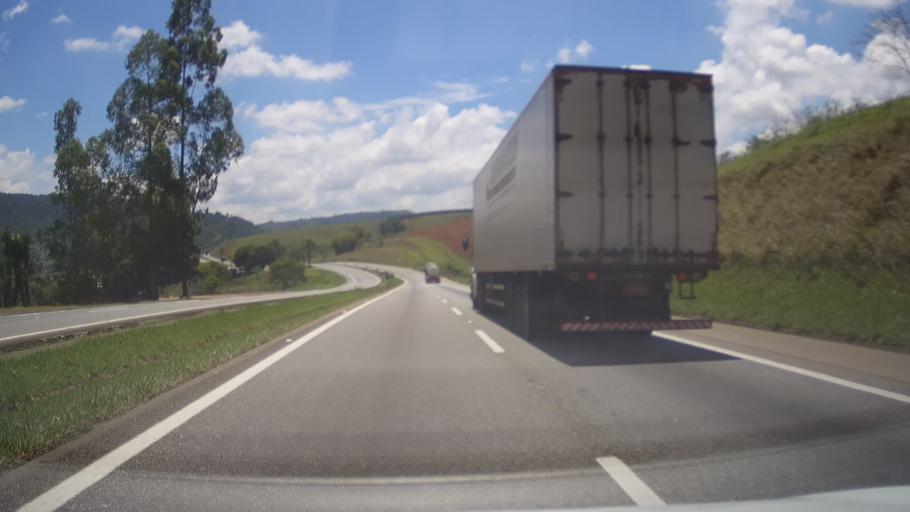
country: BR
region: Minas Gerais
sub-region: Campanha
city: Campanha
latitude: -21.8245
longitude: -45.4953
